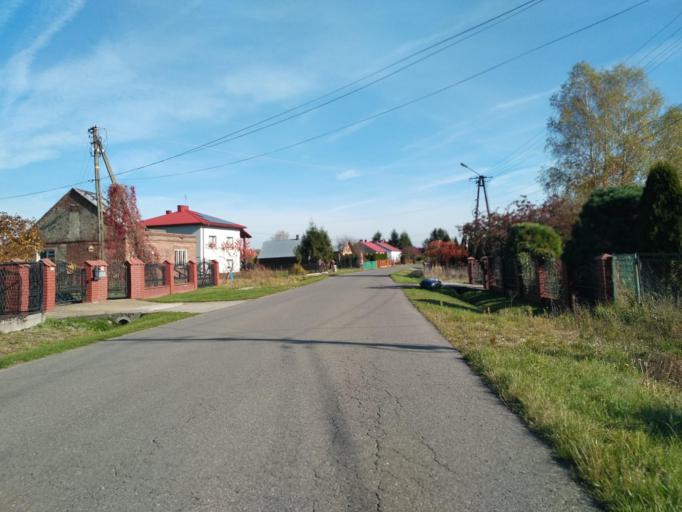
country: PL
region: Subcarpathian Voivodeship
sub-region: Powiat rzeszowski
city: Trzciana
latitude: 50.0824
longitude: 21.8096
